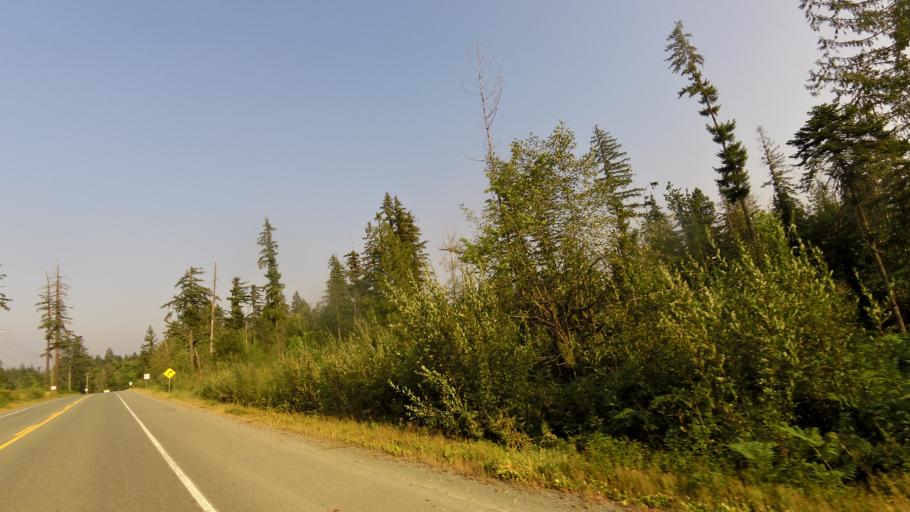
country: CA
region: British Columbia
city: Port Alberni
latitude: 49.2934
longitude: -124.9133
